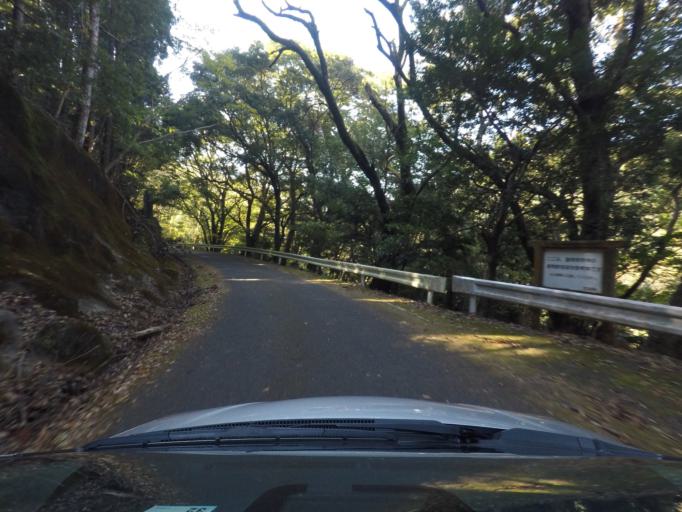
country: JP
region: Miyazaki
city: Kobayashi
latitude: 32.0240
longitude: 131.1913
